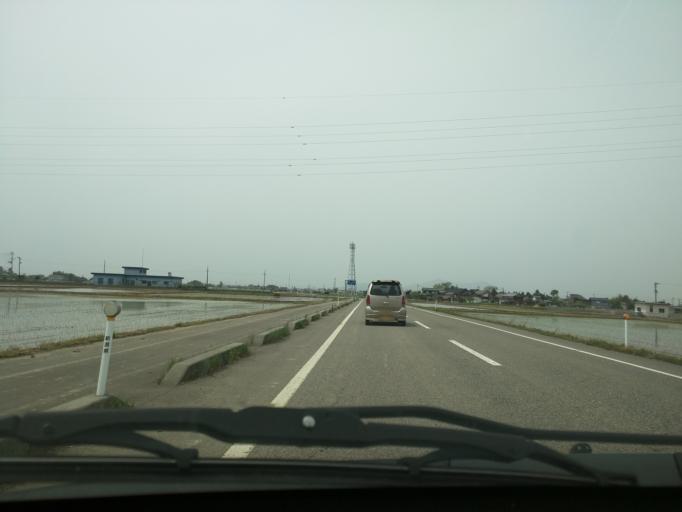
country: JP
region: Niigata
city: Mitsuke
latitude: 37.5739
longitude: 138.9439
